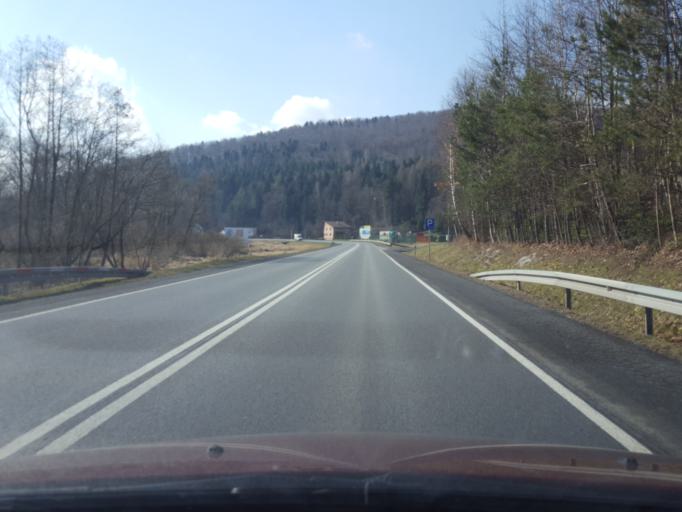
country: PL
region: Lesser Poland Voivodeship
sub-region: Powiat nowosadecki
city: Lososina Dolna
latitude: 49.7810
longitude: 20.6431
